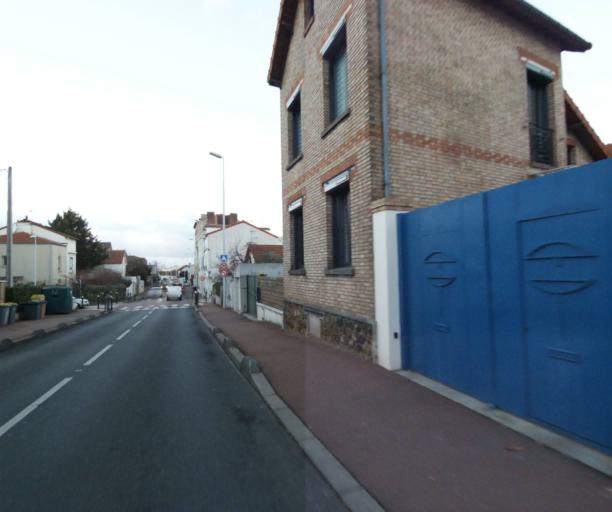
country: FR
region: Ile-de-France
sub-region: Departement des Hauts-de-Seine
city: Nanterre
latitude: 48.8837
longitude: 2.2155
